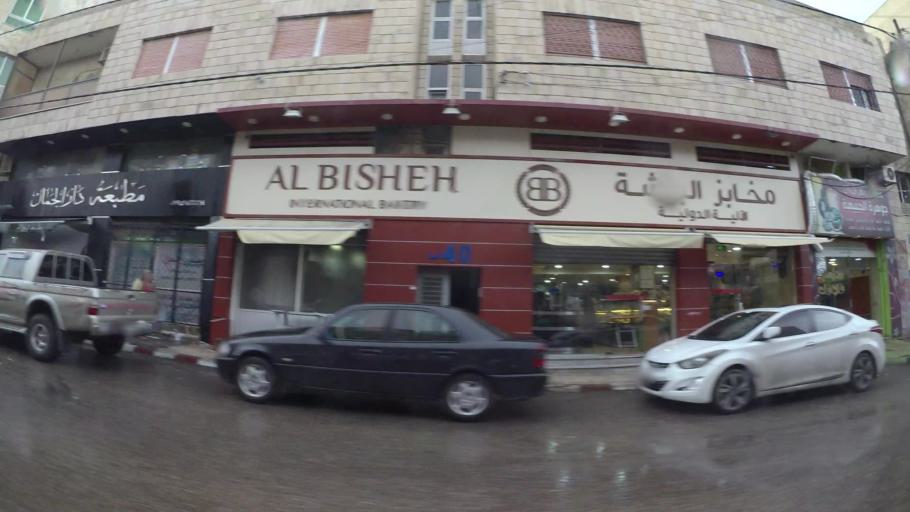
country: JO
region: Amman
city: Al Jubayhah
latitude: 32.0243
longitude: 35.8655
